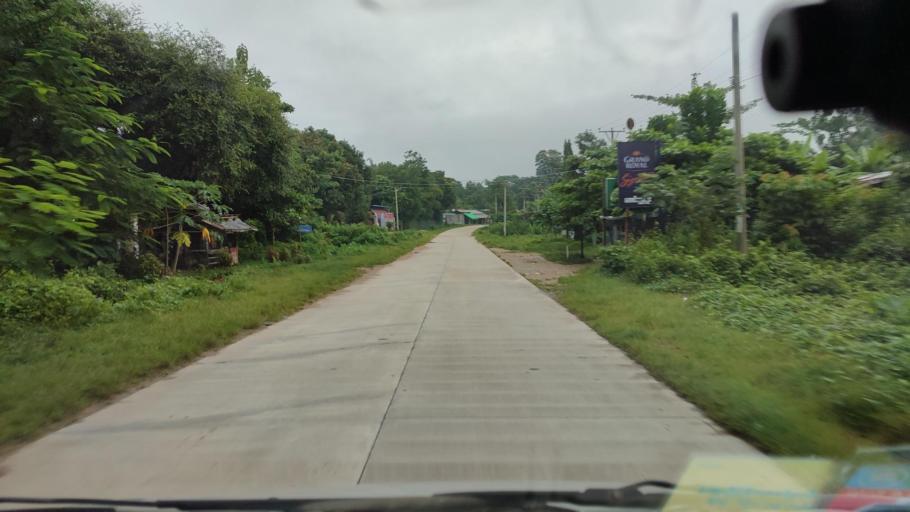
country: MM
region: Bago
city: Taungoo
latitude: 18.9703
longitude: 96.4998
